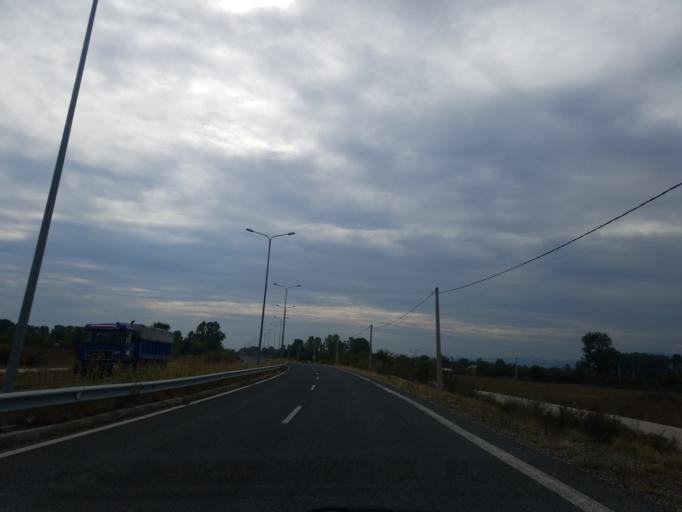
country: GR
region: Thessaly
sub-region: Trikala
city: Pyrgetos
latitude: 39.5370
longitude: 21.7368
